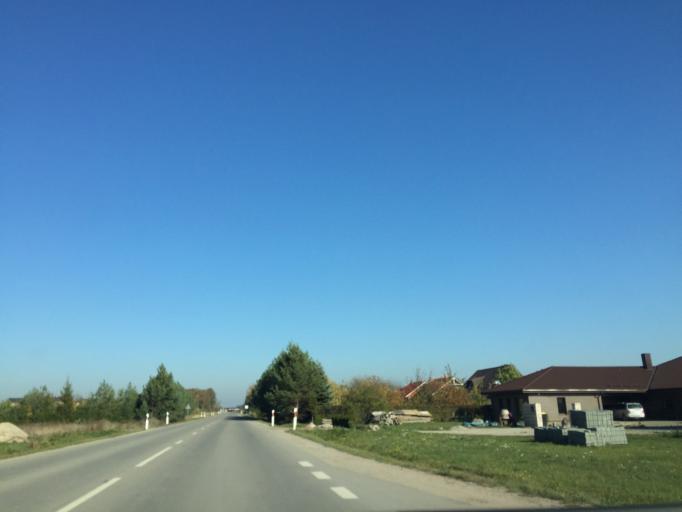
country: LT
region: Klaipedos apskritis
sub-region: Klaipeda
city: Klaipeda
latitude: 55.7563
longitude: 21.1930
